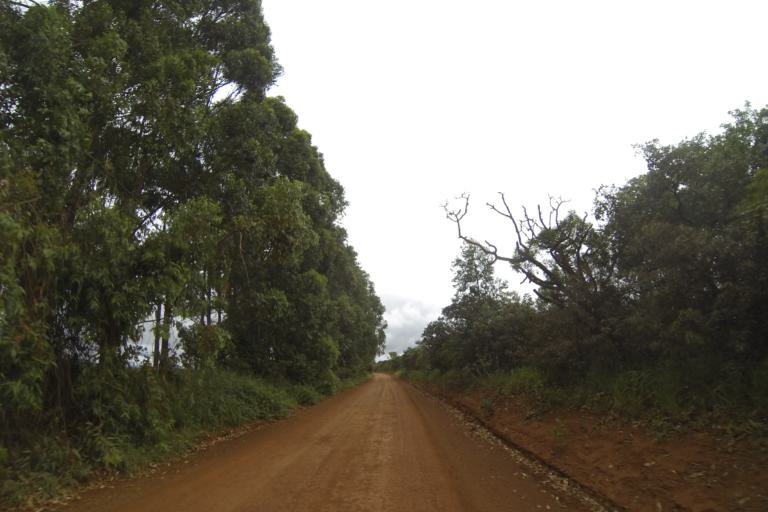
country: BR
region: Minas Gerais
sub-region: Campos Altos
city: Campos Altos
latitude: -19.8530
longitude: -46.3183
